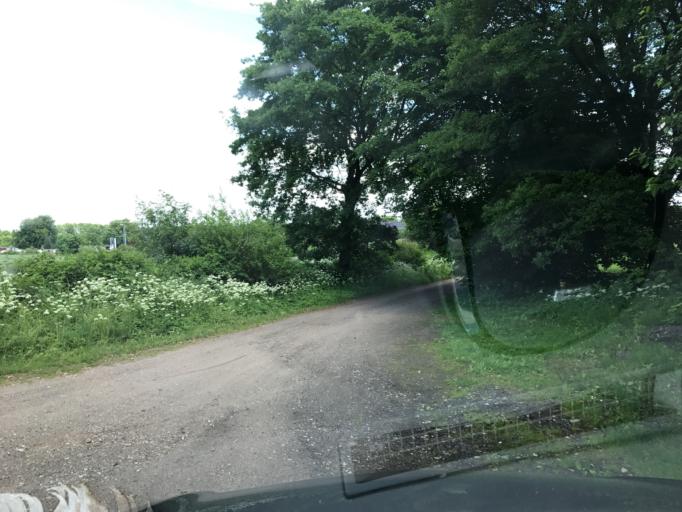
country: DE
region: Schleswig-Holstein
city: Burg
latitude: 54.0041
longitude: 9.2482
